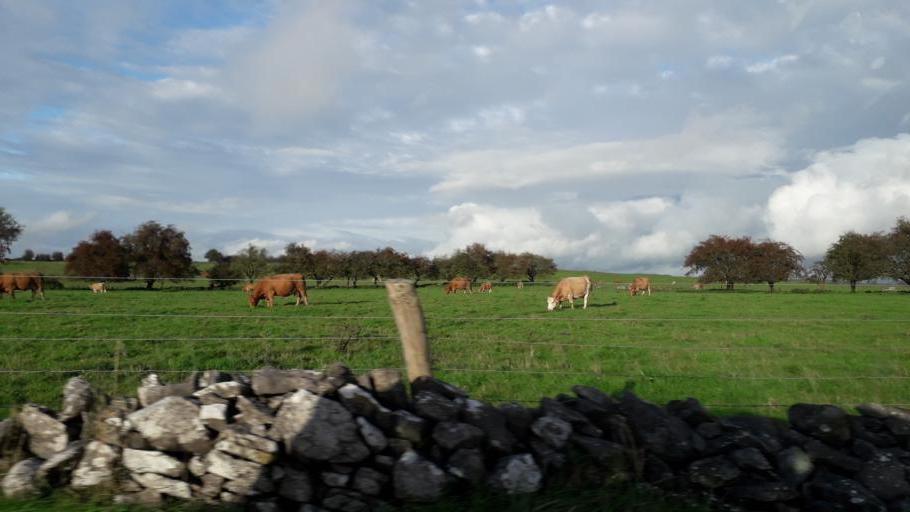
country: IE
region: Connaught
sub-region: Roscommon
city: Roscommon
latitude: 53.7698
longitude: -8.2226
